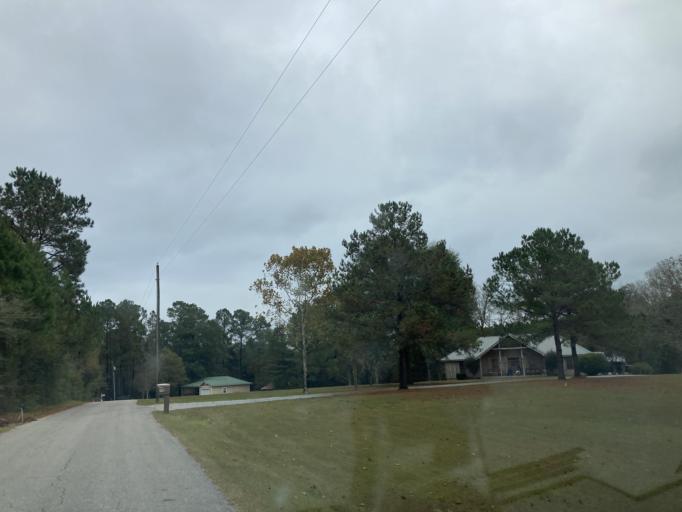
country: US
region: Mississippi
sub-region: Lamar County
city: Purvis
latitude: 31.1913
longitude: -89.4270
